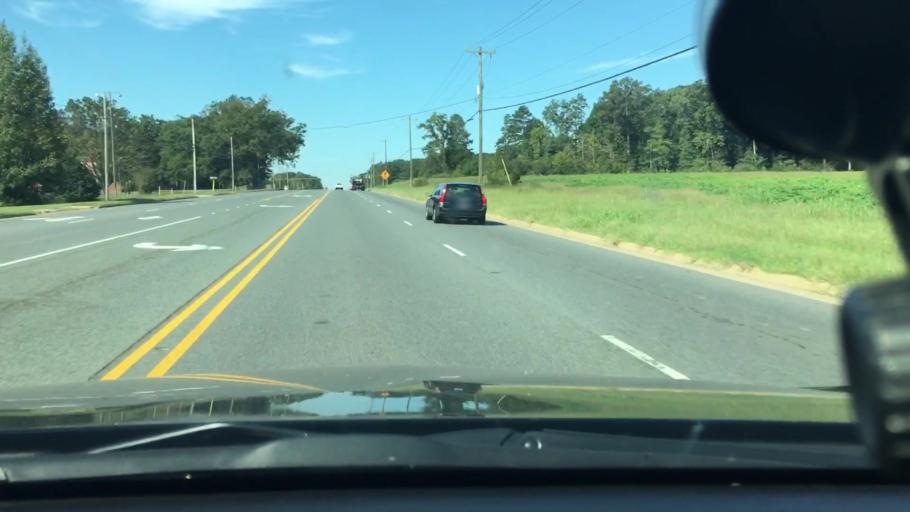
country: US
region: North Carolina
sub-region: Cabarrus County
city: Midland
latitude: 35.2496
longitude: -80.5336
